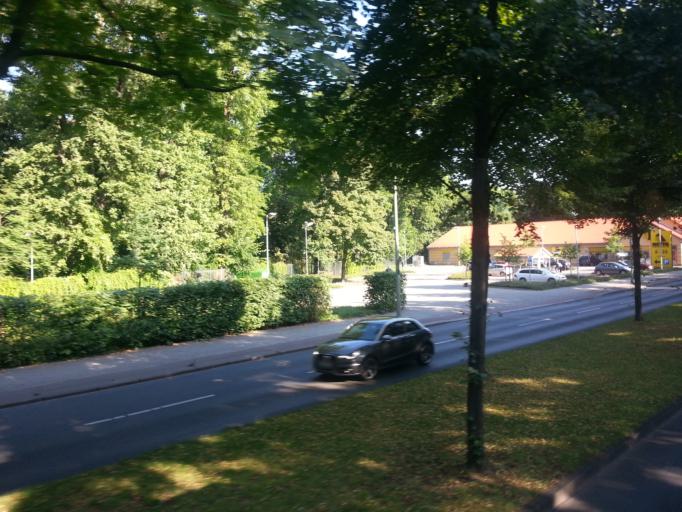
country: DE
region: Berlin
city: Reinickendorf
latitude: 52.5801
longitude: 13.3337
